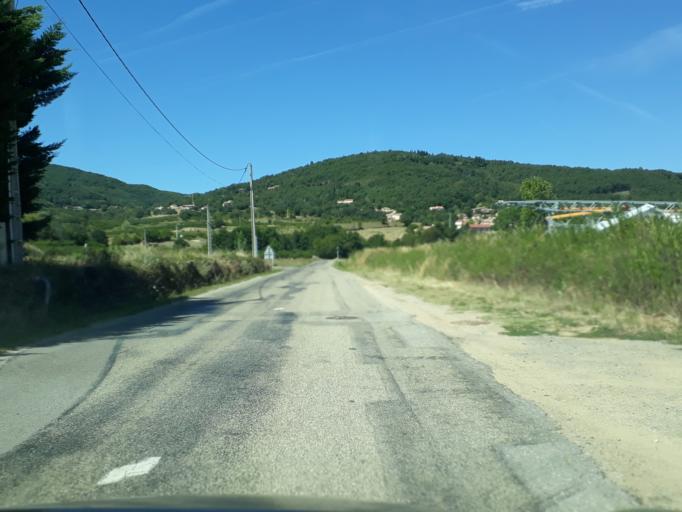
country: FR
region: Rhone-Alpes
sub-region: Departement de l'Ardeche
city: Felines
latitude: 45.3056
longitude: 4.7327
